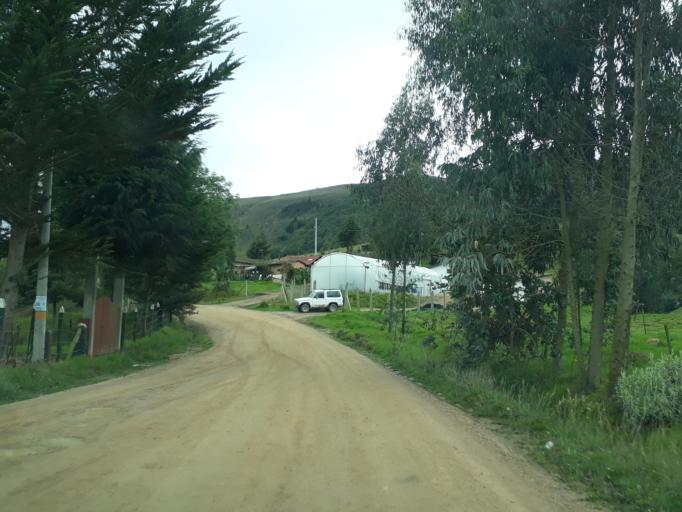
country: CO
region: Cundinamarca
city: Cucunuba
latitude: 5.2030
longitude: -73.7738
